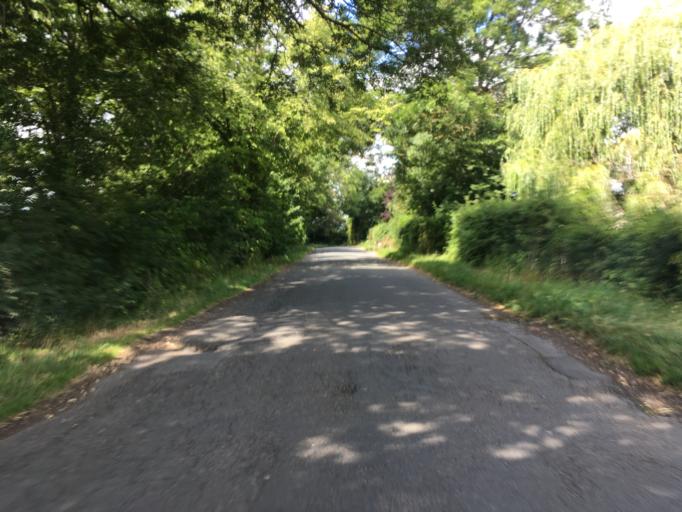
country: GB
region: England
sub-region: Gloucestershire
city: Gloucester
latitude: 51.9088
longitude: -2.2304
